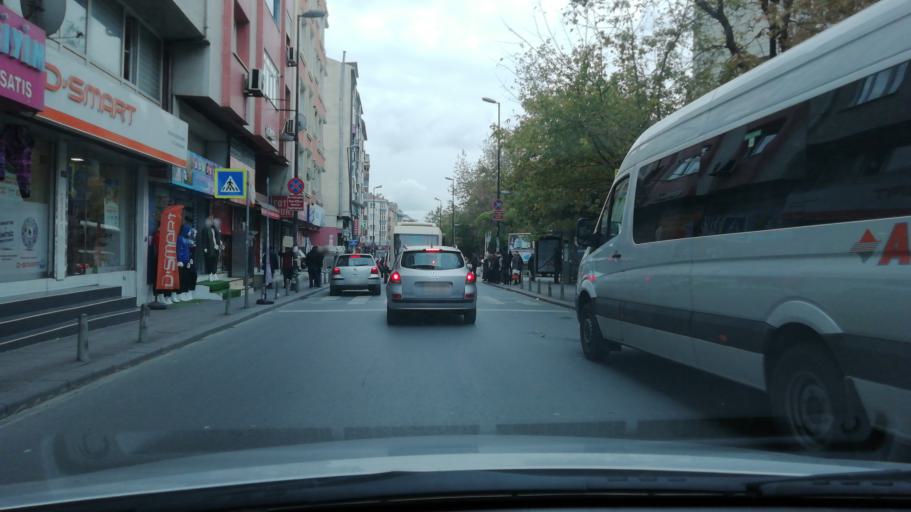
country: TR
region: Istanbul
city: Bahcelievler
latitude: 41.0034
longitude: 28.8387
